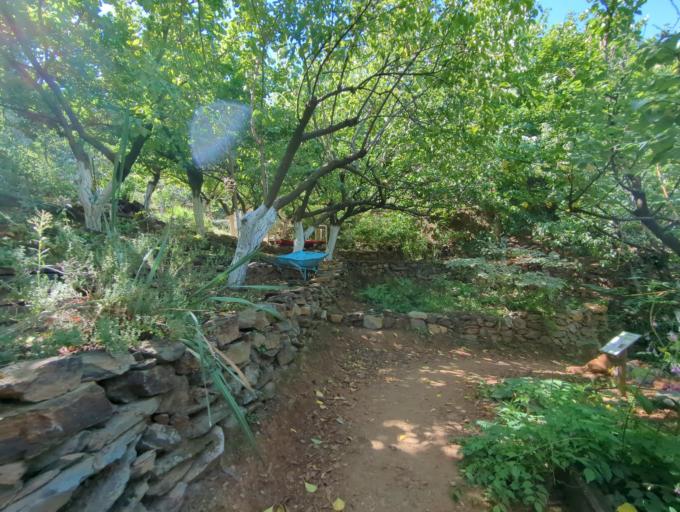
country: GR
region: Crete
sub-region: Nomos Chanias
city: Galatas
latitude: 35.4194
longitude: 23.9399
